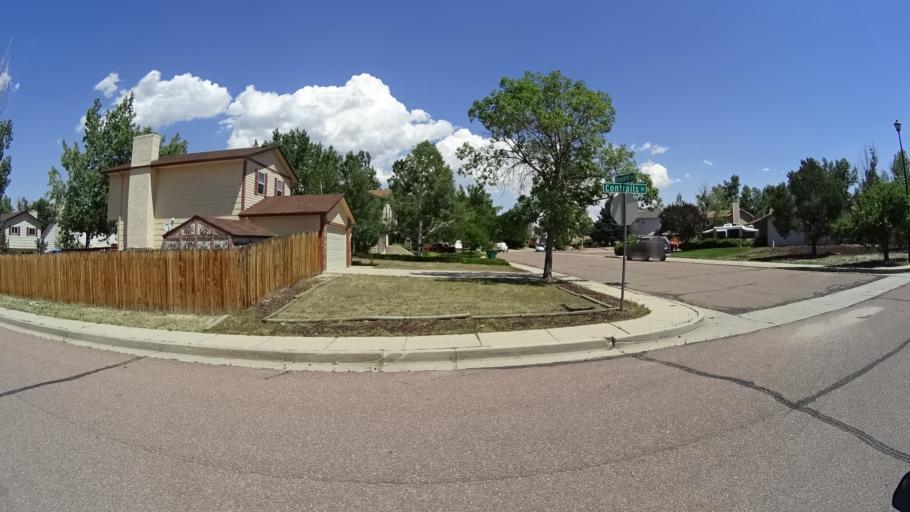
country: US
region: Colorado
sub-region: El Paso County
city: Black Forest
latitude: 38.9509
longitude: -104.7552
